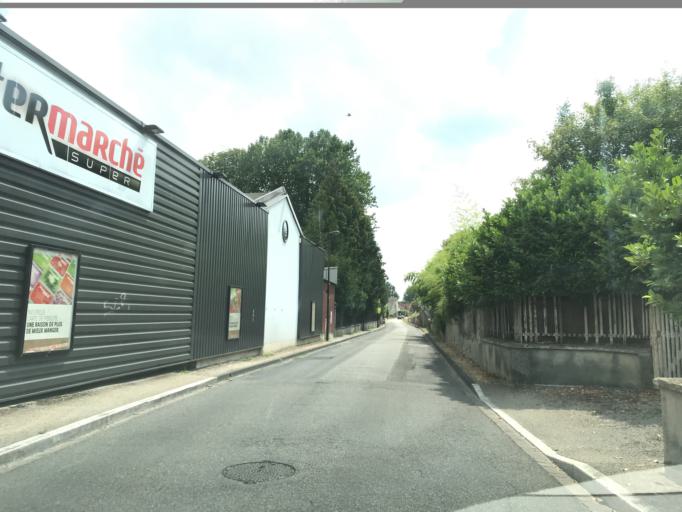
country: FR
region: Haute-Normandie
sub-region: Departement de l'Eure
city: Ivry-la-Bataille
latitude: 48.8819
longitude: 1.4588
